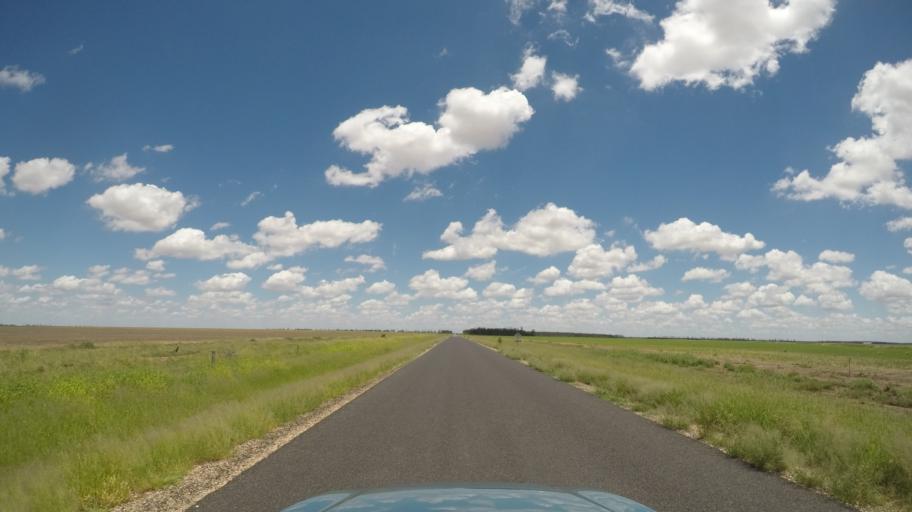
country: AU
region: Queensland
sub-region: Goondiwindi
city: Goondiwindi
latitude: -28.1752
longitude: 150.2501
